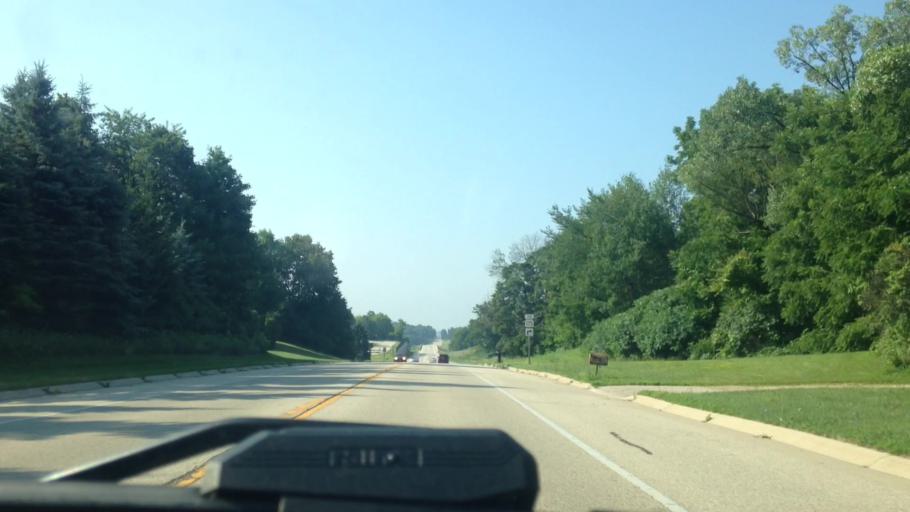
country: US
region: Wisconsin
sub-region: Washington County
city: Slinger
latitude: 43.3188
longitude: -88.2607
